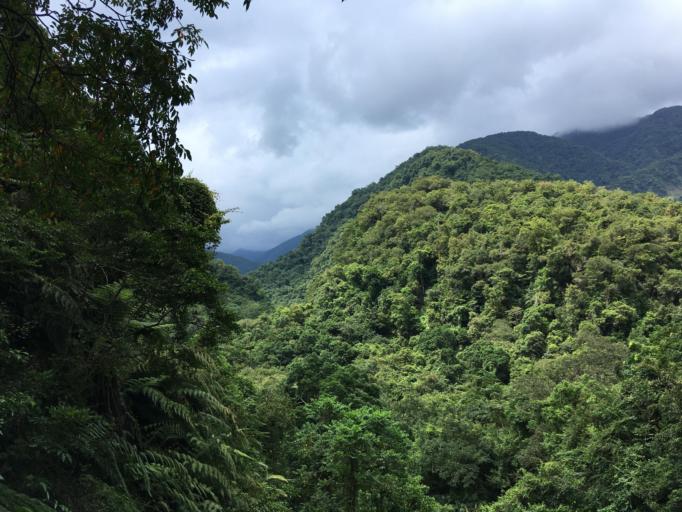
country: TW
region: Taiwan
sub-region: Yilan
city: Yilan
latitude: 24.4218
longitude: 121.6981
